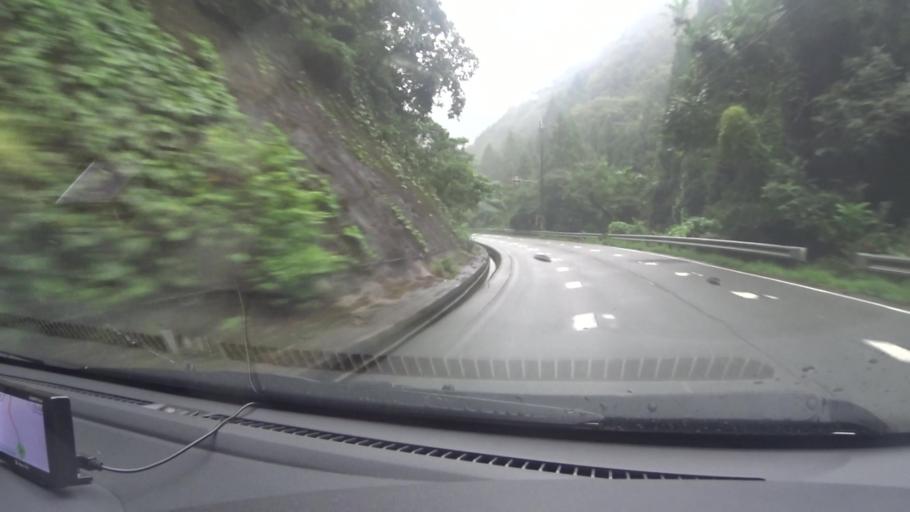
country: JP
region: Kyoto
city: Ayabe
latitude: 35.2404
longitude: 135.2978
